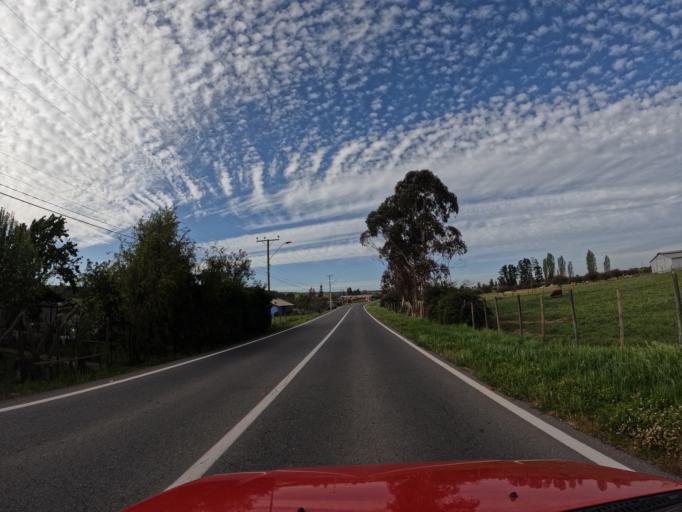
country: CL
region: O'Higgins
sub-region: Provincia de Colchagua
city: Santa Cruz
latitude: -34.2259
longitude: -71.7243
